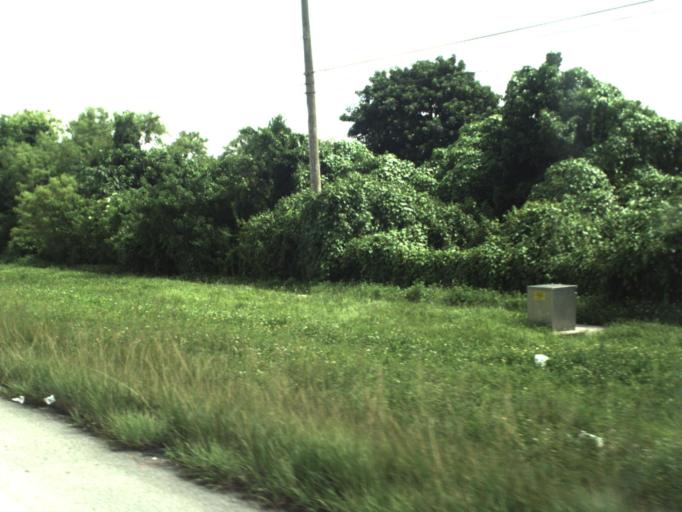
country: US
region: Florida
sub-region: Broward County
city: Southwest Ranches
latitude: 26.0656
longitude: -80.3134
